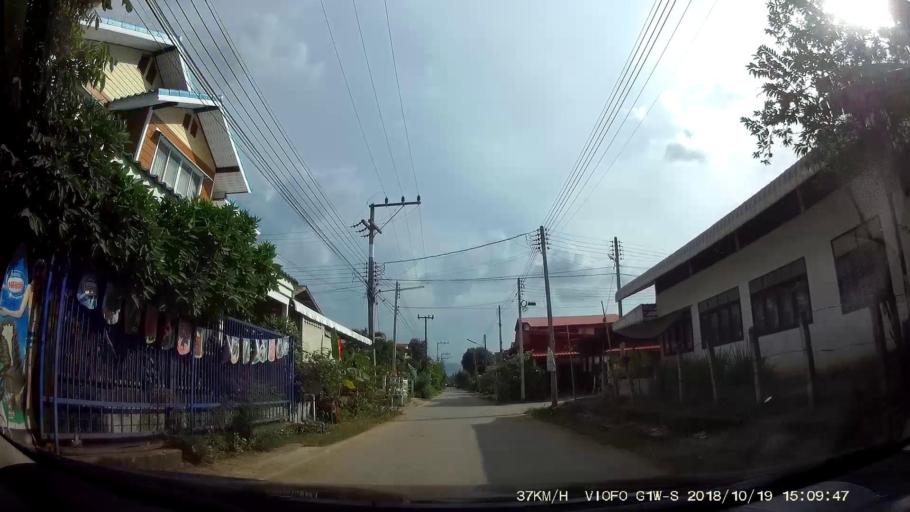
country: TH
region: Chaiyaphum
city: Phu Khiao
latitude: 16.4087
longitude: 102.1033
